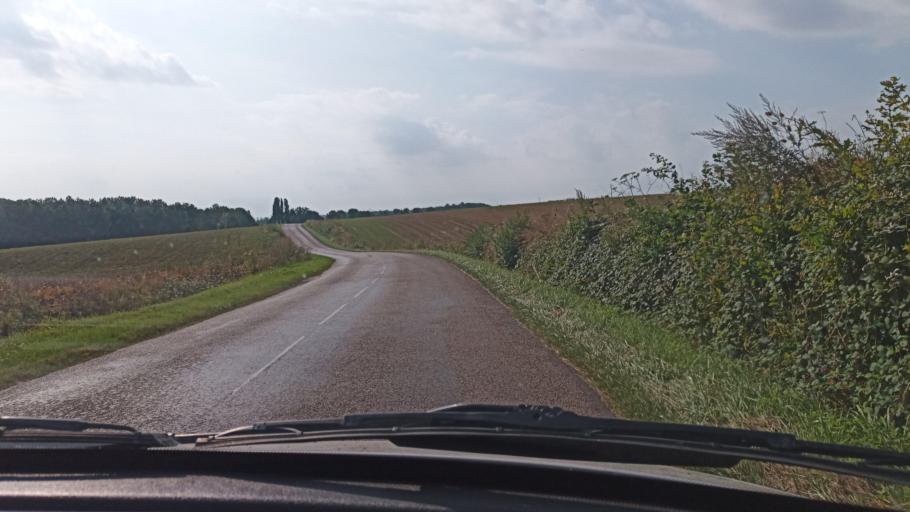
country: FR
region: Bourgogne
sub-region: Departement de l'Yonne
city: Saint-Valerien
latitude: 48.2056
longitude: 3.0766
